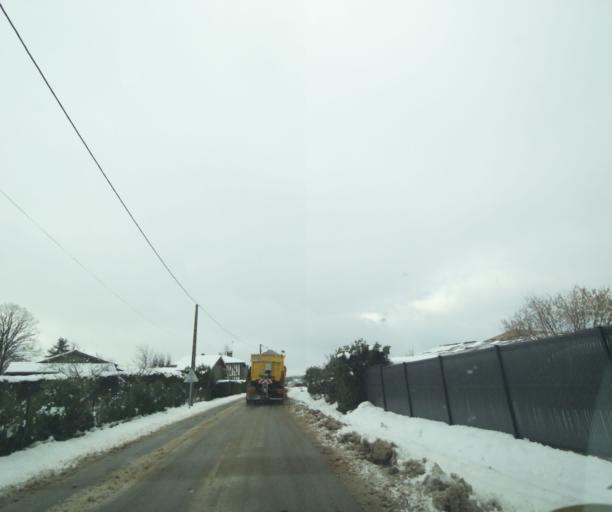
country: FR
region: Champagne-Ardenne
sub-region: Departement de la Haute-Marne
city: Montier-en-Der
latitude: 48.4934
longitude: 4.7009
